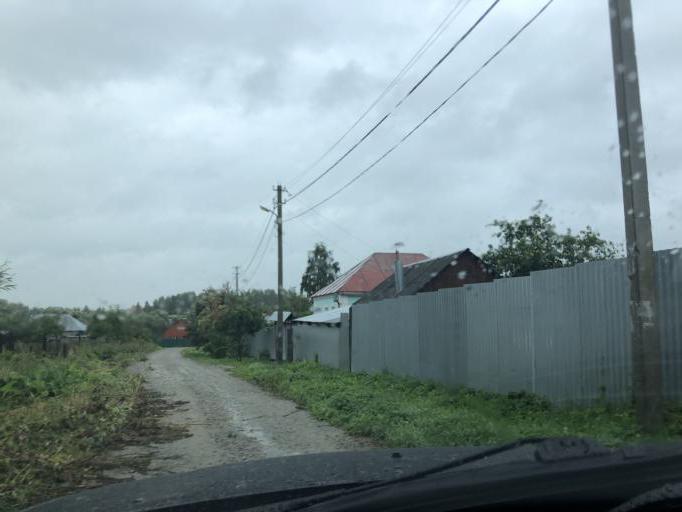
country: RU
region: Tula
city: Gorelki
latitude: 54.2604
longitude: 37.6189
